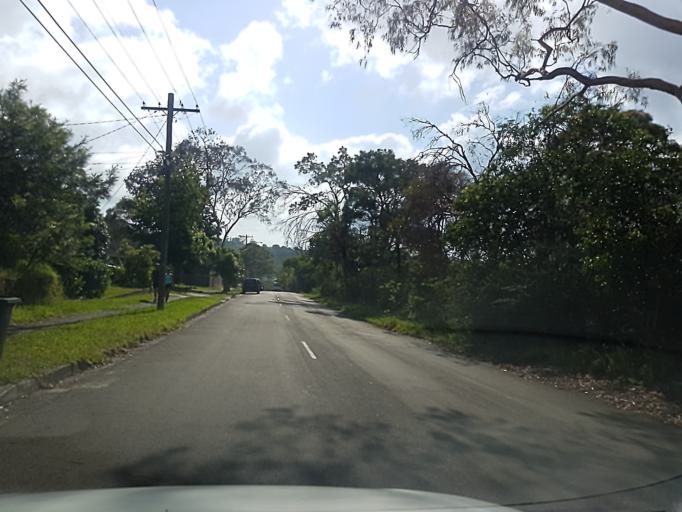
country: AU
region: New South Wales
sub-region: Warringah
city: Davidson
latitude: -33.7472
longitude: 151.2072
